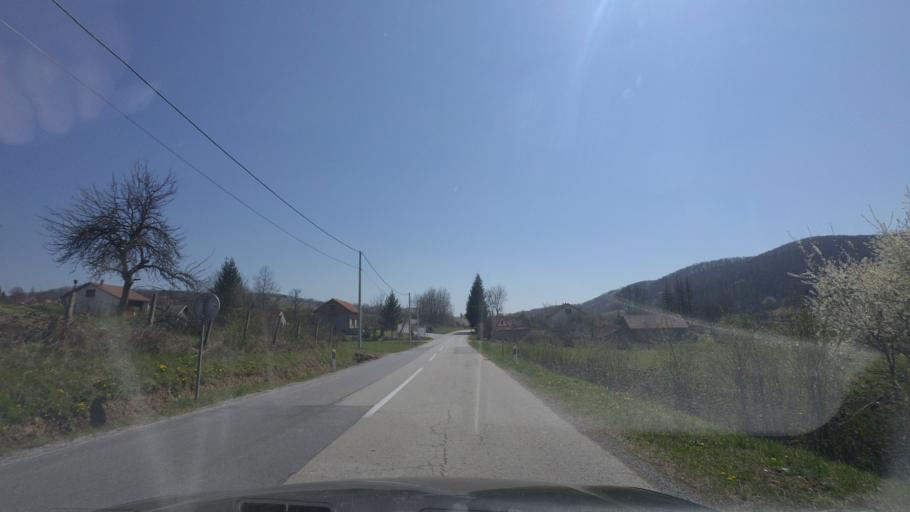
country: HR
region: Karlovacka
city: Vojnic
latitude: 45.3626
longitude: 15.6662
